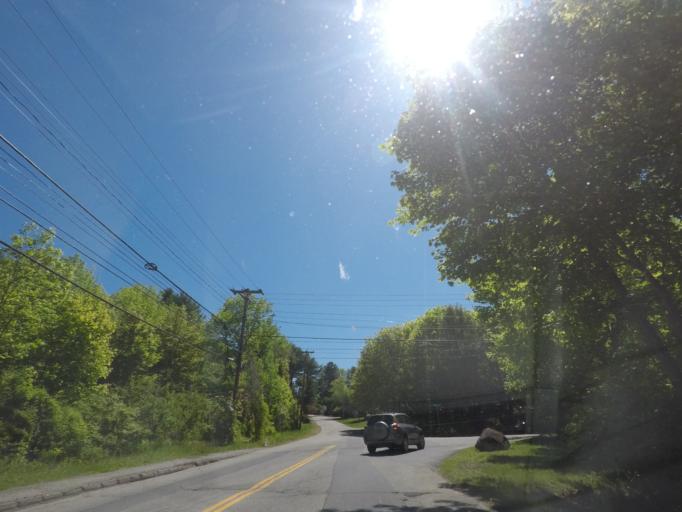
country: US
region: Maine
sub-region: Kennebec County
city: Augusta
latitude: 44.3184
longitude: -69.8029
